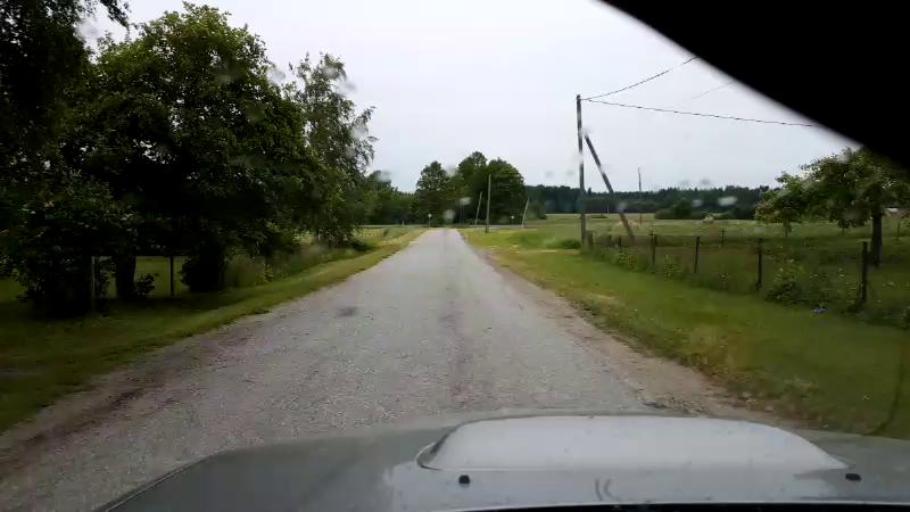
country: EE
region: Paernumaa
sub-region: Halinga vald
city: Parnu-Jaagupi
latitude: 58.5290
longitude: 24.5868
